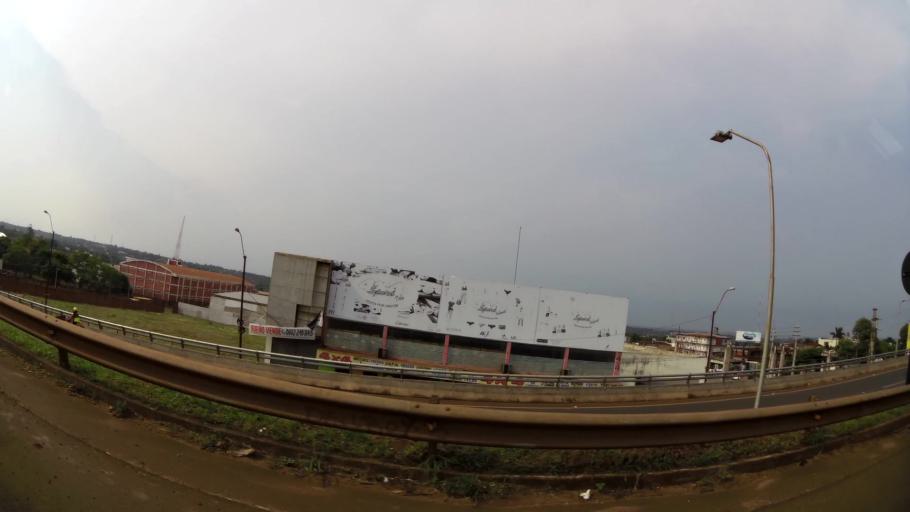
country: PY
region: Alto Parana
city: Ciudad del Este
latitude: -25.5067
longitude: -54.6394
